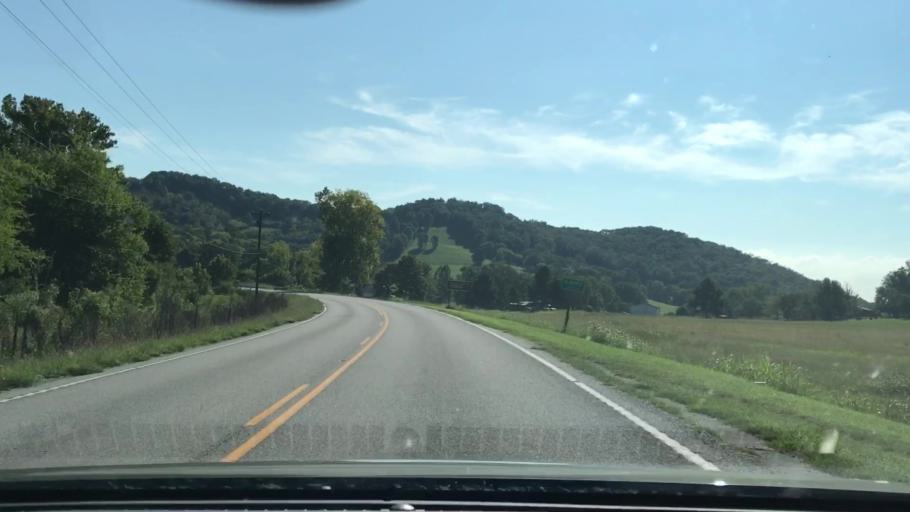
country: US
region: Tennessee
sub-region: Jackson County
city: Gainesboro
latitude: 36.3458
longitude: -85.8104
